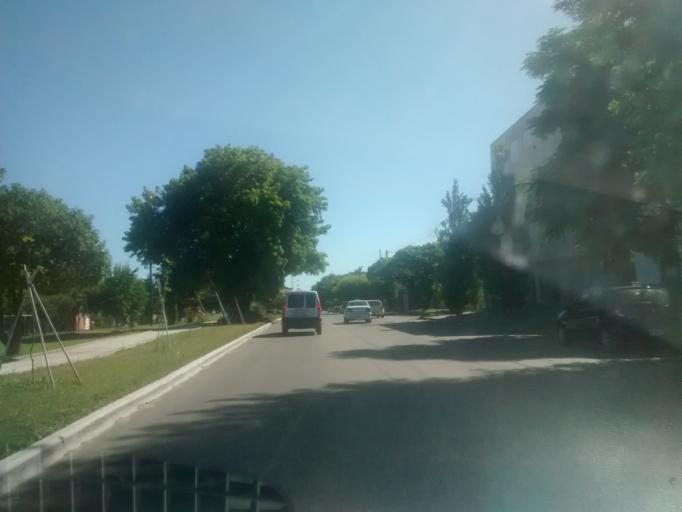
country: AR
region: Buenos Aires
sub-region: Partido de La Plata
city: La Plata
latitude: -34.9269
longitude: -57.9234
